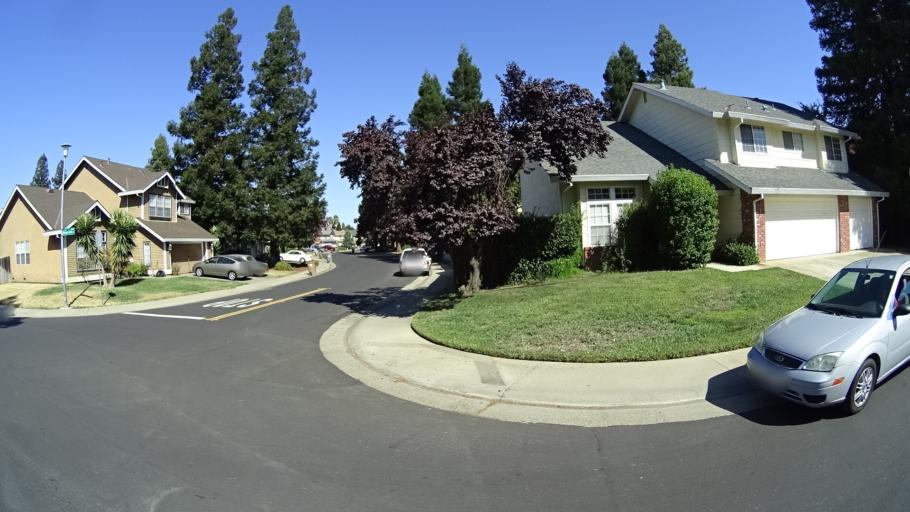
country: US
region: California
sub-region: Sacramento County
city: Laguna
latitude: 38.4239
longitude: -121.4368
